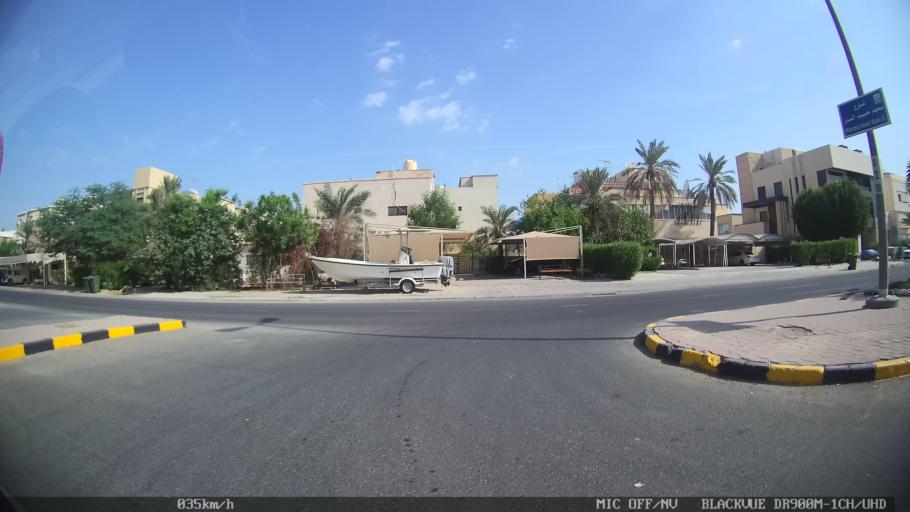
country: KW
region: Al Asimah
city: Ad Dasmah
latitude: 29.3508
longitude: 47.9982
